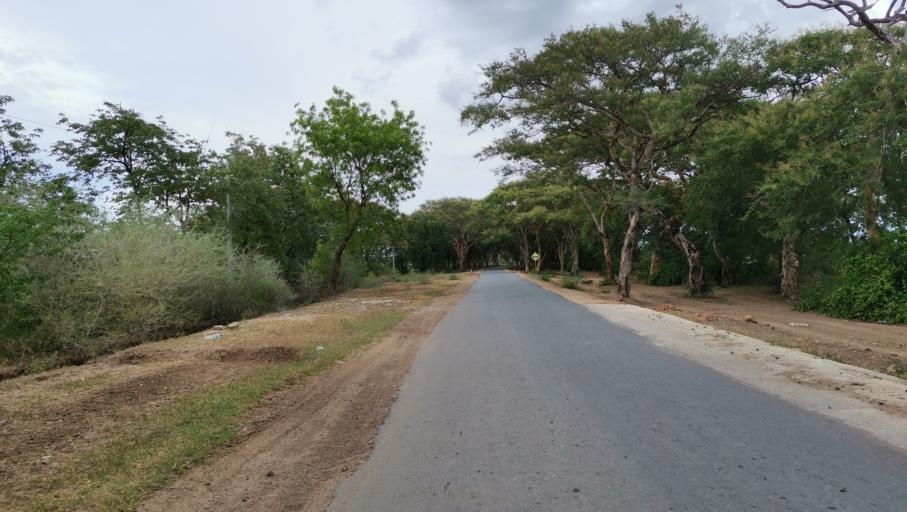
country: MM
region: Sagain
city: Monywa
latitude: 21.8509
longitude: 95.4324
